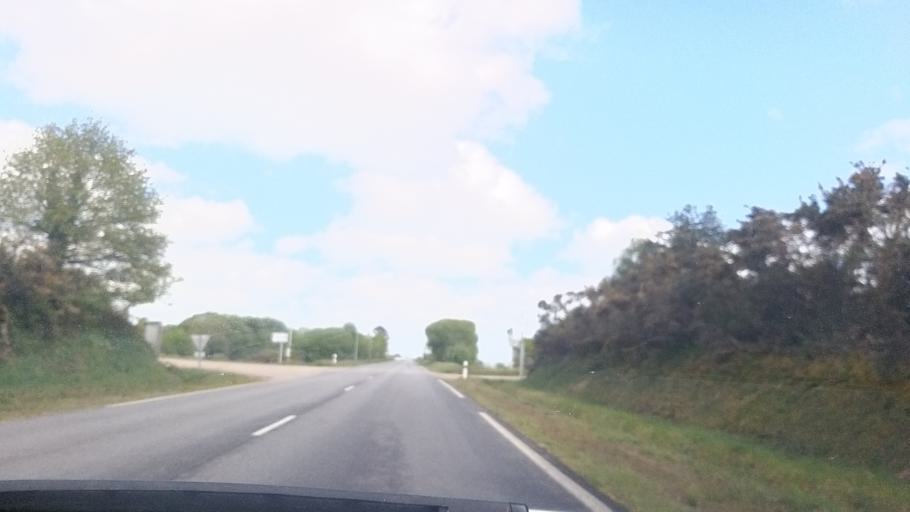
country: FR
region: Brittany
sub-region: Departement du Finistere
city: Huelgoat
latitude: 48.3455
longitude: -3.7417
